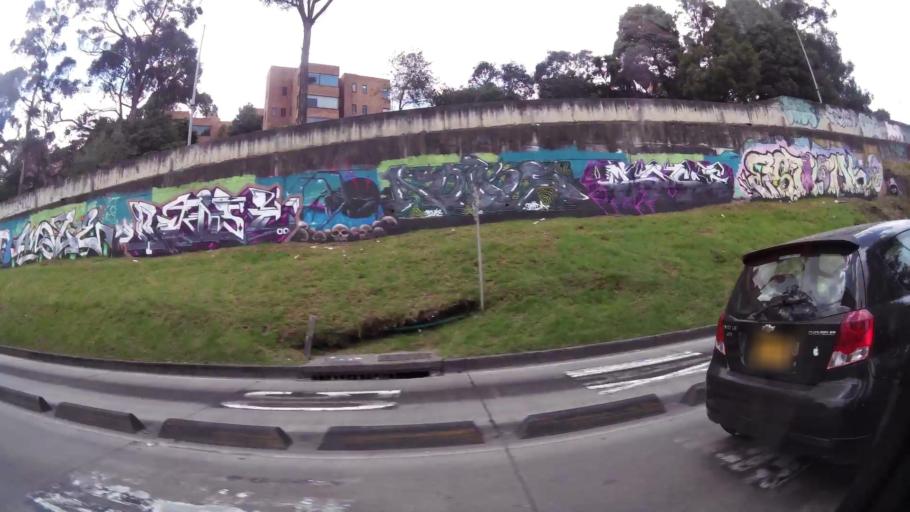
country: CO
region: Cundinamarca
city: Cota
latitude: 4.7317
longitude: -74.0749
